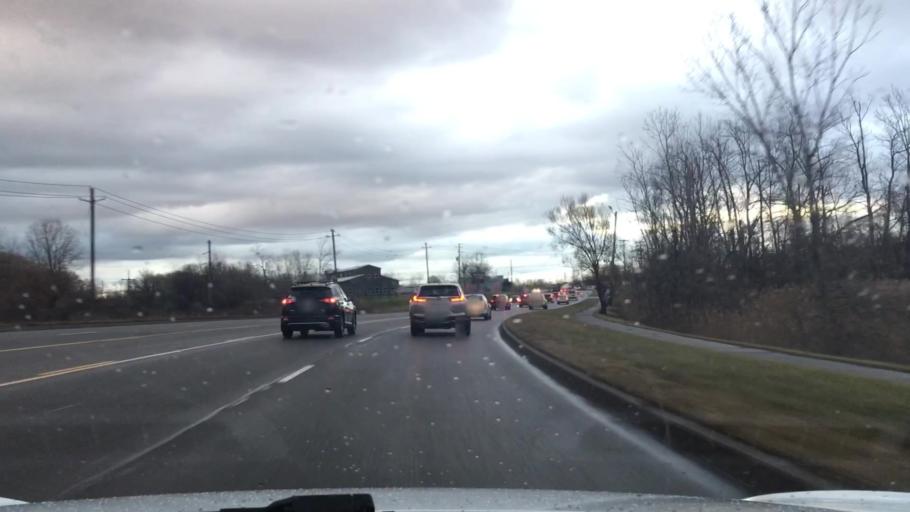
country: US
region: New York
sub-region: Erie County
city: Depew
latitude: 42.9370
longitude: -78.7097
